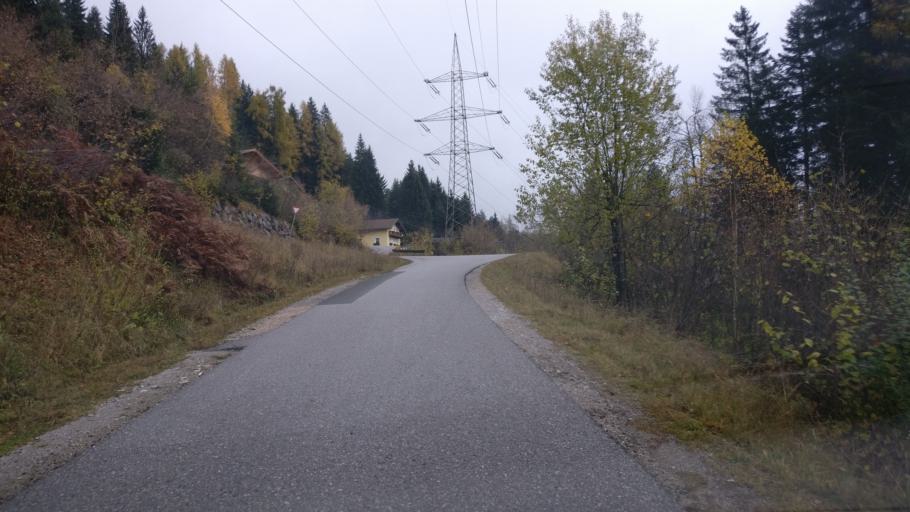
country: AT
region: Salzburg
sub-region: Politischer Bezirk Sankt Johann im Pongau
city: Forstau
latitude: 47.3967
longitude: 13.5129
